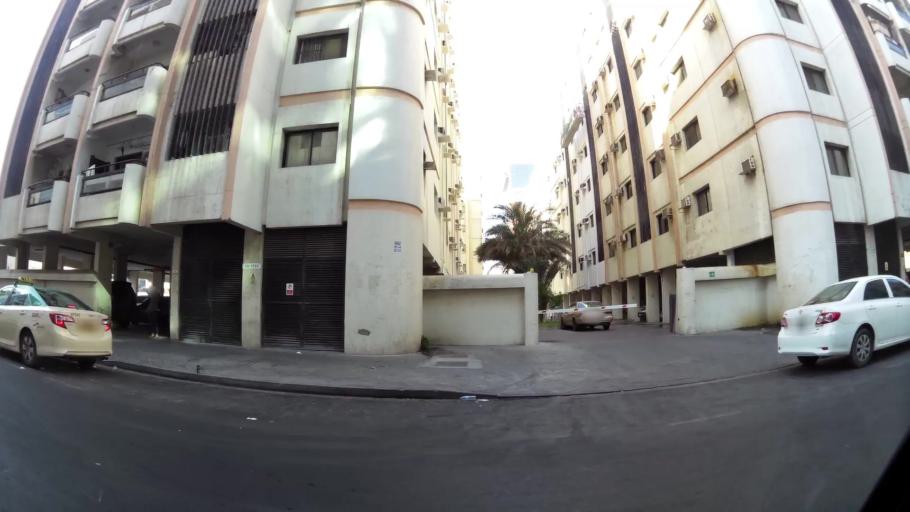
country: AE
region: Ash Shariqah
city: Sharjah
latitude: 25.2651
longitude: 55.3251
